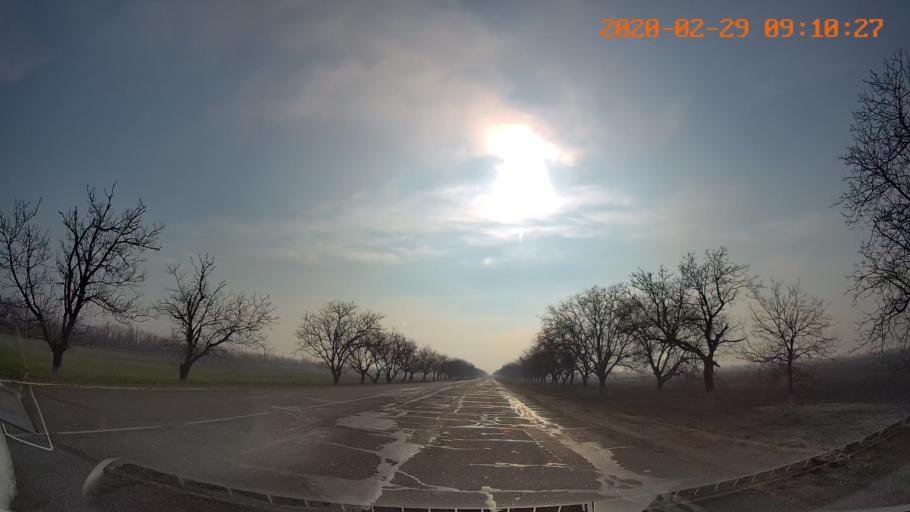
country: MD
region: Telenesti
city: Slobozia
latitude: 46.8439
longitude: 29.7823
